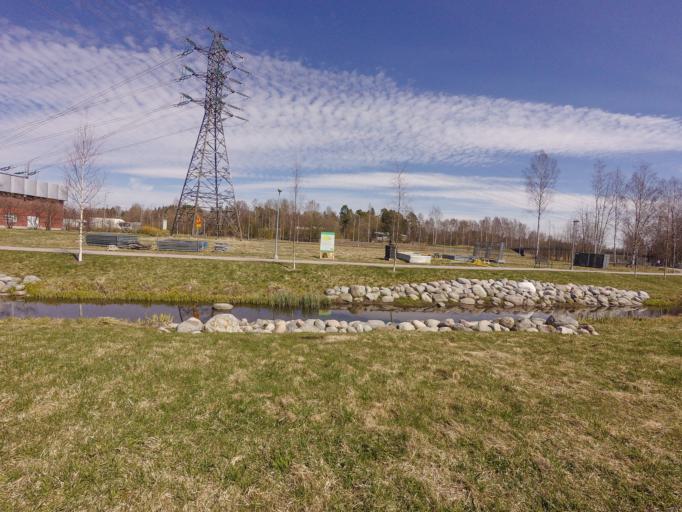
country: FI
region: Uusimaa
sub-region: Helsinki
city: Vantaa
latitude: 60.2317
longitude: 25.1114
